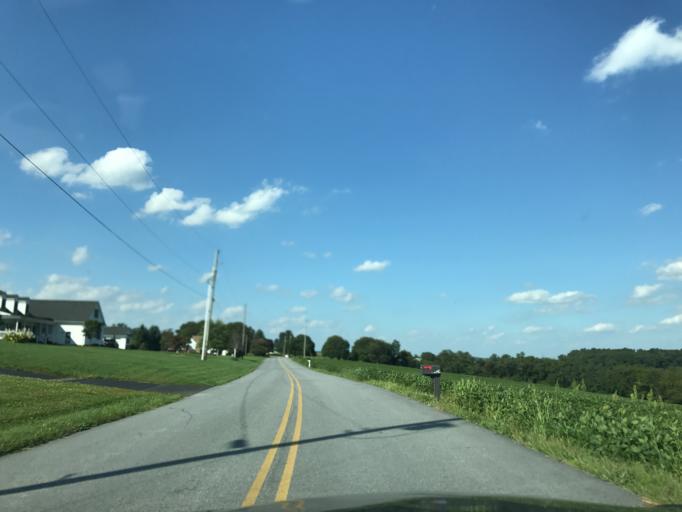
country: US
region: Pennsylvania
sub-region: York County
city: Stewartstown
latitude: 39.7247
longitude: -76.5853
